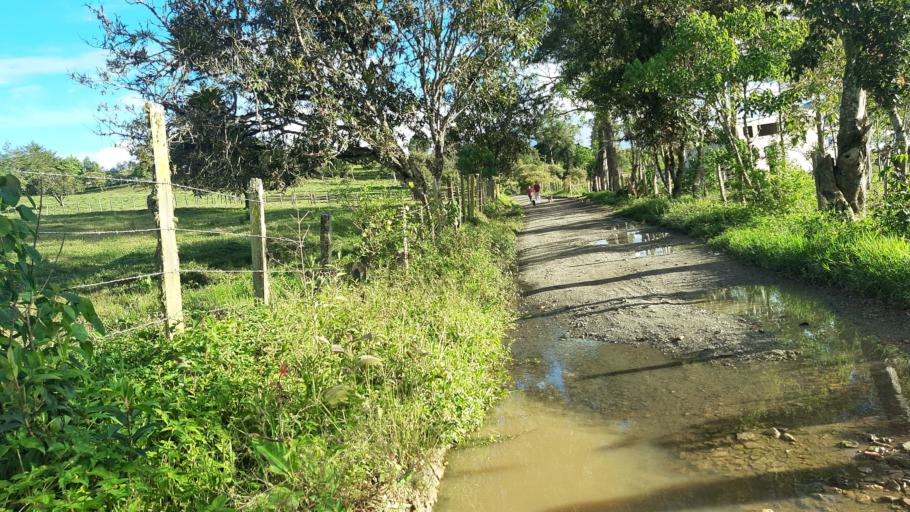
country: CO
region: Boyaca
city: Garagoa
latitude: 5.0903
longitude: -73.3614
